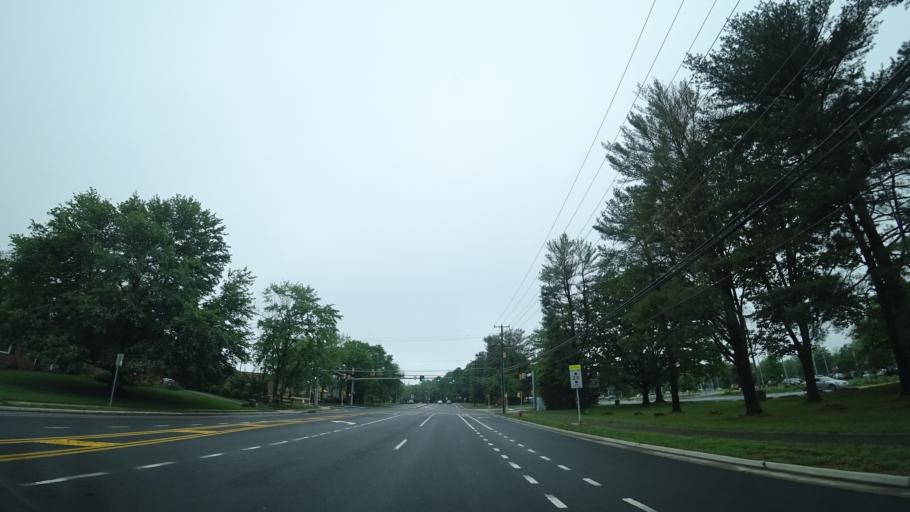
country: US
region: Virginia
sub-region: Fairfax County
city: Tysons Corner
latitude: 38.9406
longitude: -77.2271
